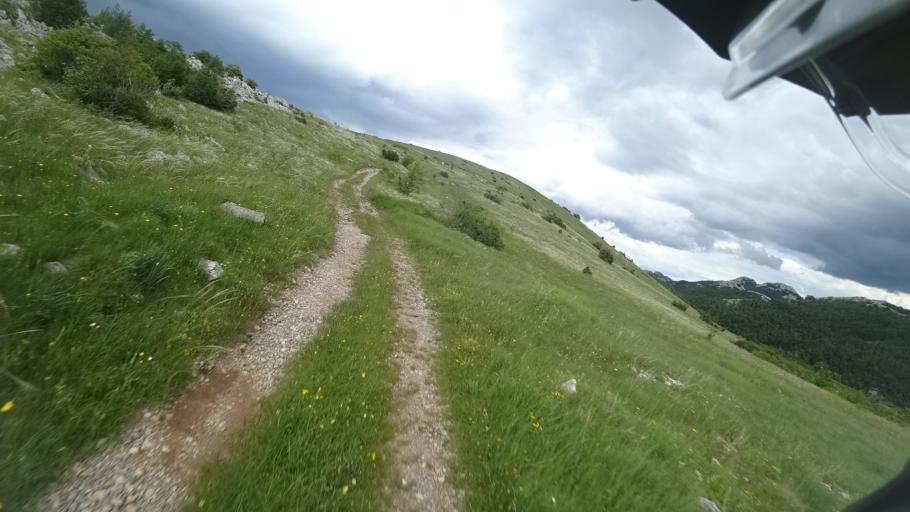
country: HR
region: Zadarska
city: Obrovac
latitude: 44.2675
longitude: 15.7267
